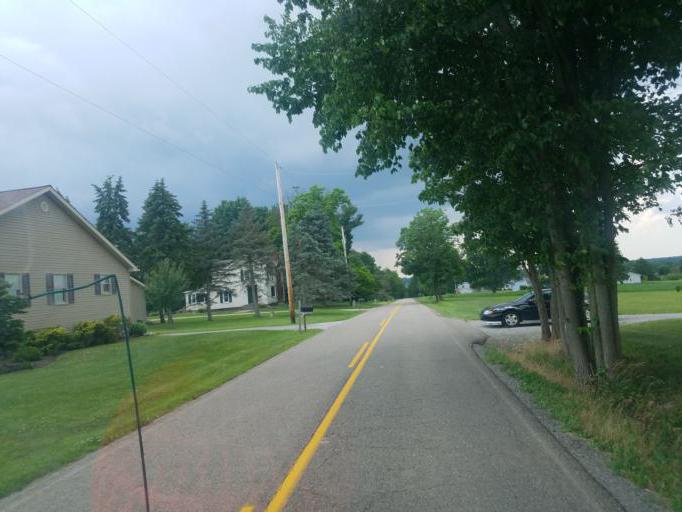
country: US
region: Ohio
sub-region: Mahoning County
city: Sebring
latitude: 40.9741
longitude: -80.9428
